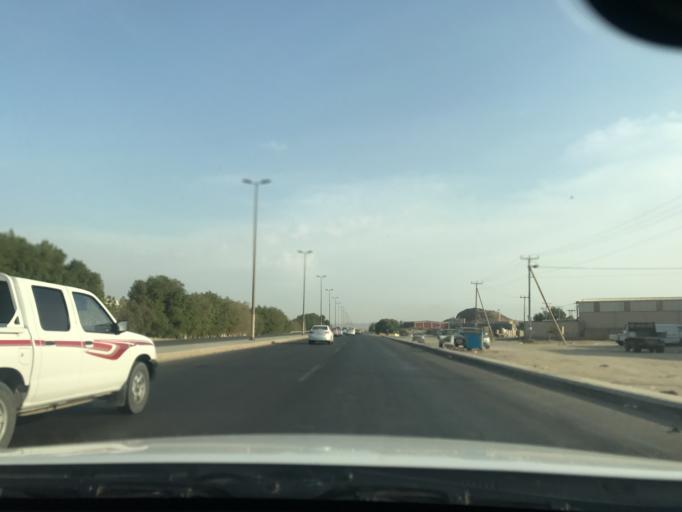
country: SA
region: Makkah
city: Jeddah
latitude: 21.4033
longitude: 39.4268
